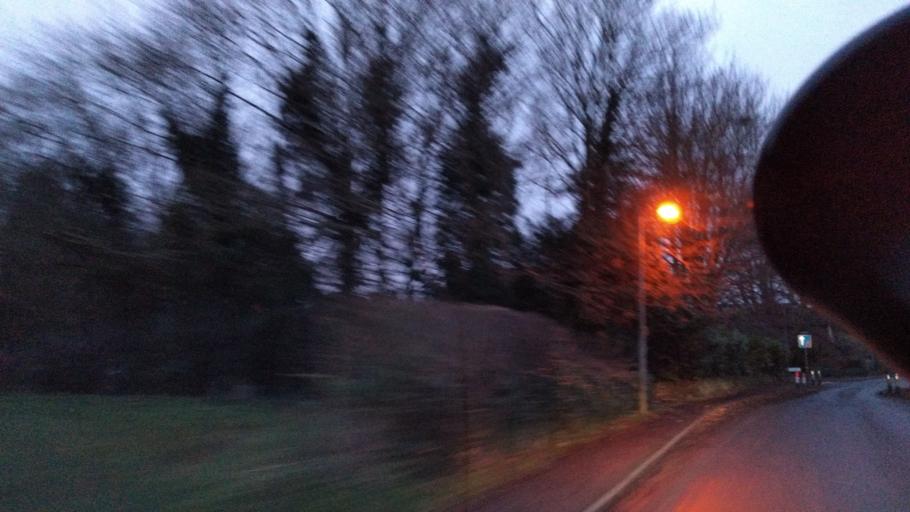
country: GB
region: England
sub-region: Borough of Swindon
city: Highworth
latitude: 51.5880
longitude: -1.7245
